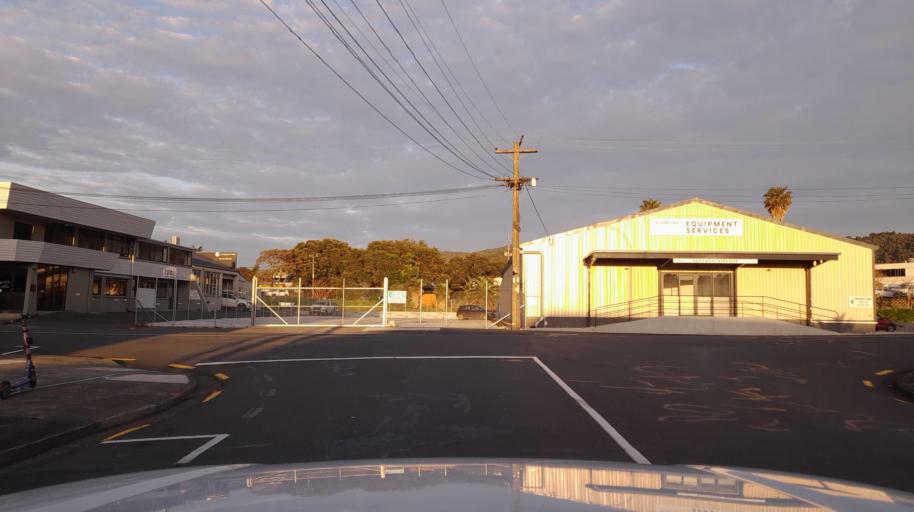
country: NZ
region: Northland
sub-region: Whangarei
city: Whangarei
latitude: -35.7289
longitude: 174.3218
